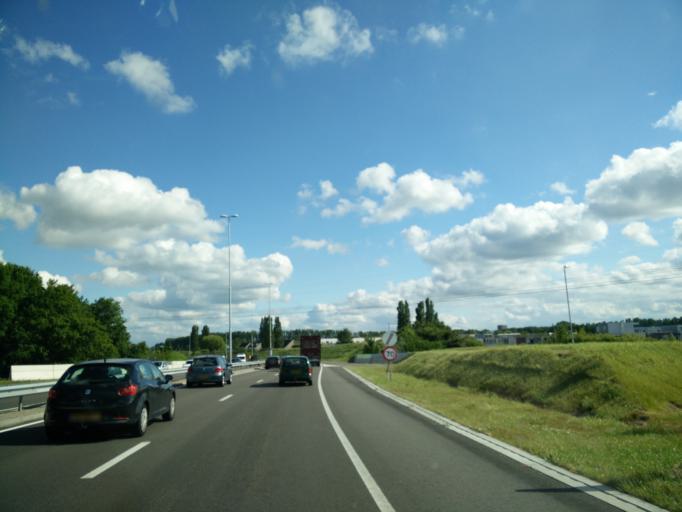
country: NL
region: Groningen
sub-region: Gemeente Groningen
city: Korrewegwijk
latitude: 53.2458
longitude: 6.5817
